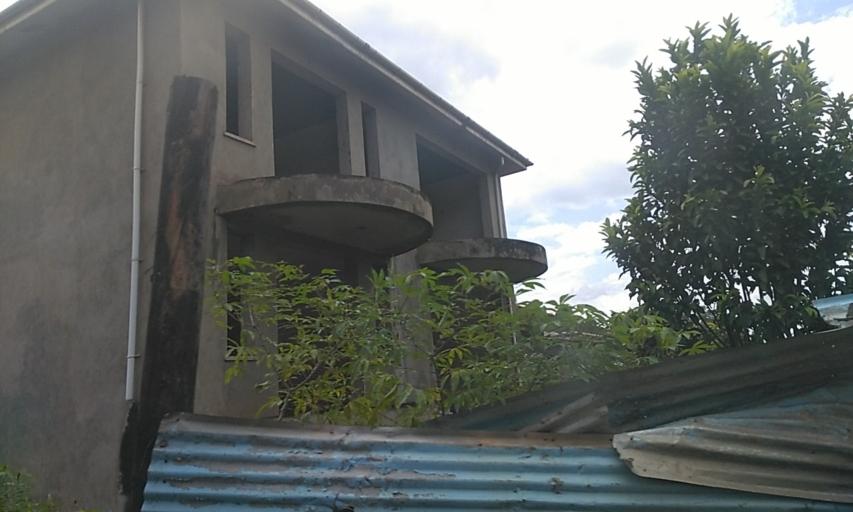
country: UG
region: Central Region
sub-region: Kampala District
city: Kampala
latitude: 0.3309
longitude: 32.5907
